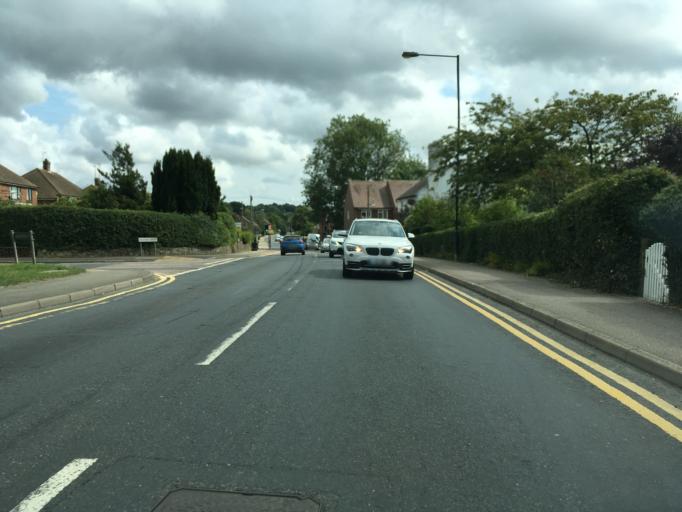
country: GB
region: England
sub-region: Kent
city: Tenterden
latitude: 51.0857
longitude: 0.6909
